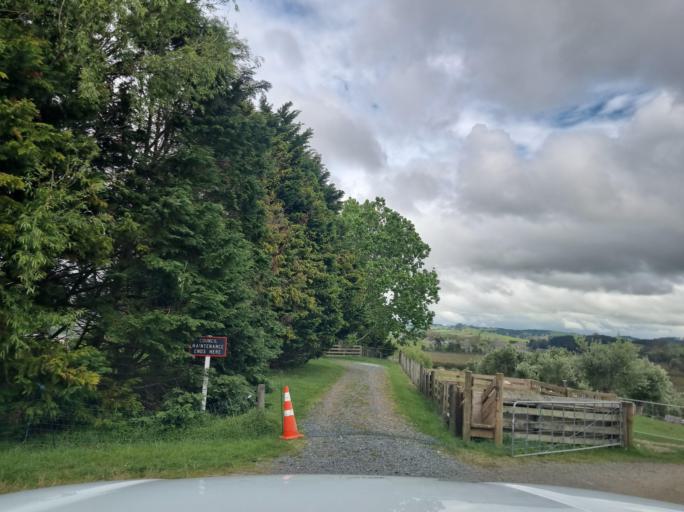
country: NZ
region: Northland
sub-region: Whangarei
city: Ruakaka
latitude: -36.1278
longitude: 174.2032
